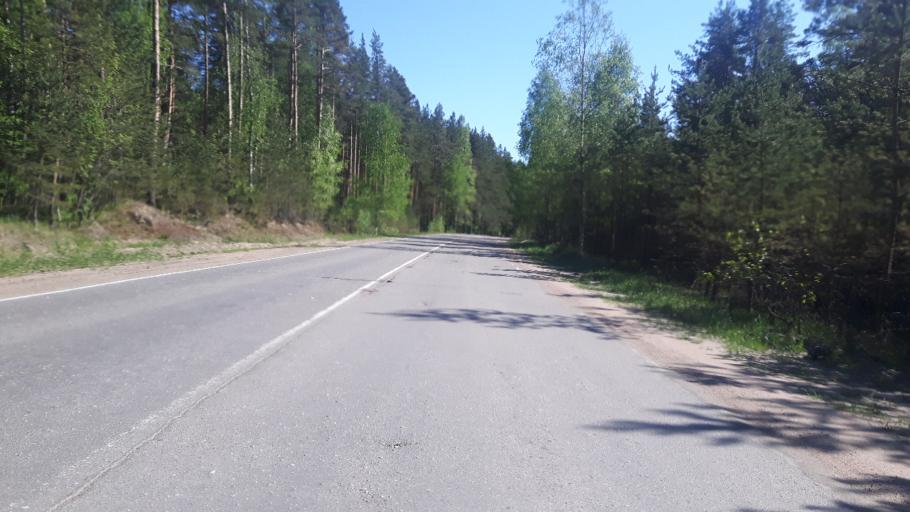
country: RU
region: Leningrad
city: Glebychevo
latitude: 60.2409
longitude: 29.0020
